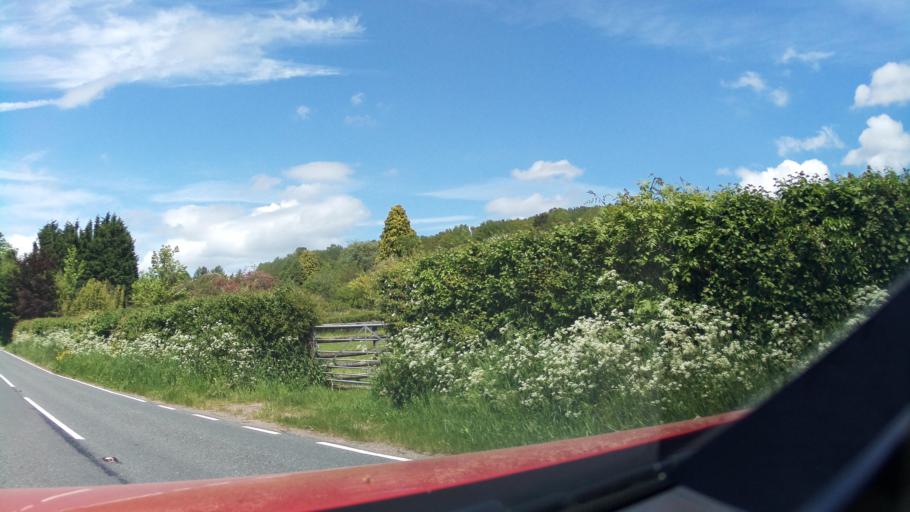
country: GB
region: Wales
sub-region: Monmouthshire
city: Mitchel Troy
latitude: 51.7555
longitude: -2.7220
